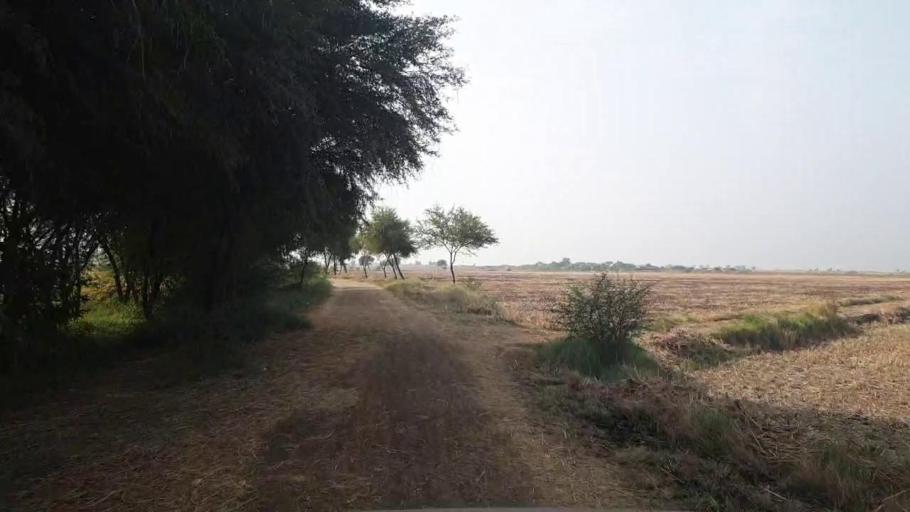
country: PK
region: Sindh
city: Tando Muhammad Khan
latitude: 25.1046
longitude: 68.5019
